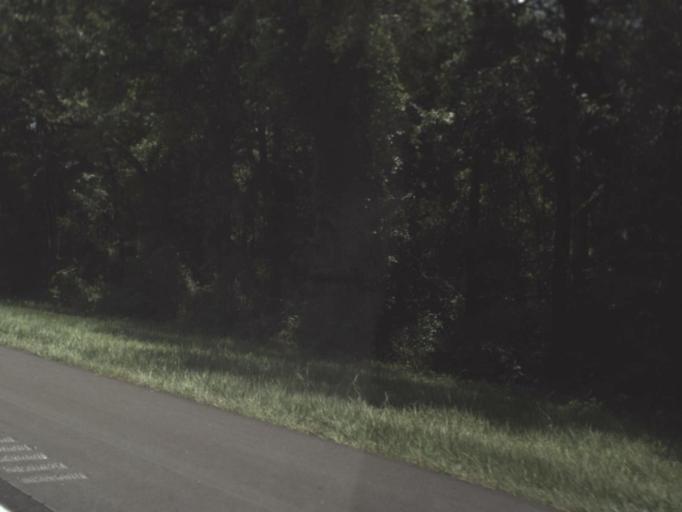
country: US
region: Florida
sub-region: Madison County
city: Madison
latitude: 30.4064
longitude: -83.4043
